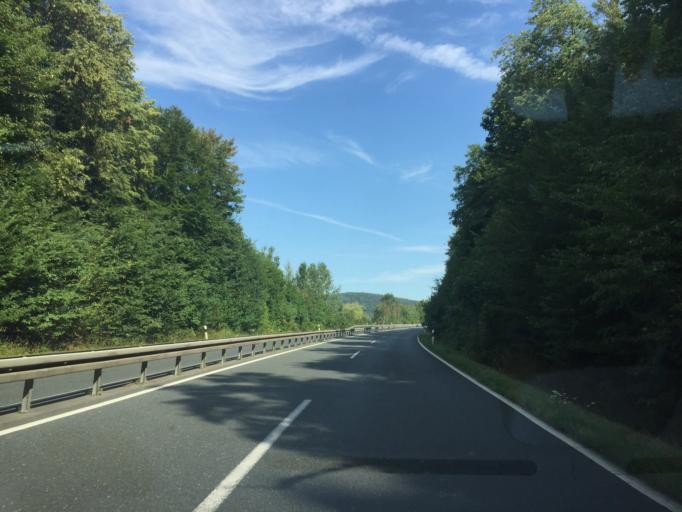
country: DE
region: Lower Saxony
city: Gittelde
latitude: 51.8042
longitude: 10.1891
